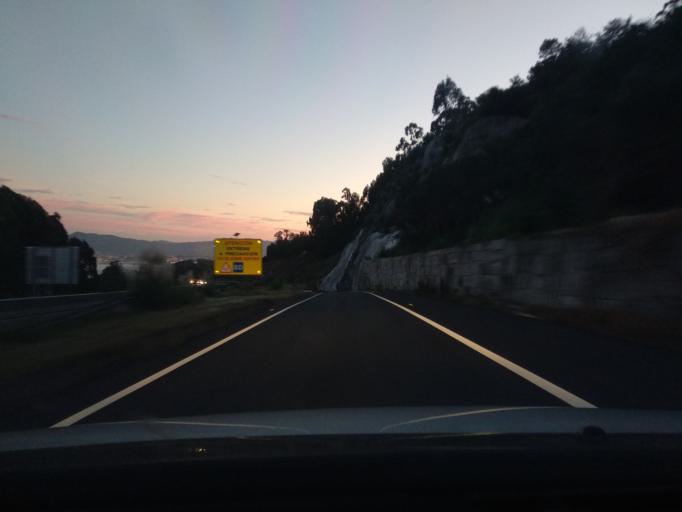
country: ES
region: Galicia
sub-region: Provincia de Pontevedra
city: Moana
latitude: 42.2913
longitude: -8.7536
